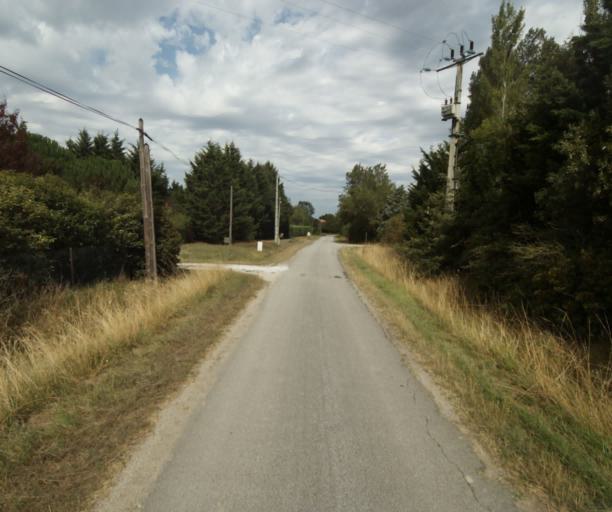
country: FR
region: Midi-Pyrenees
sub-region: Departement de la Haute-Garonne
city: Saint-Felix-Lauragais
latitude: 43.4317
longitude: 1.9422
